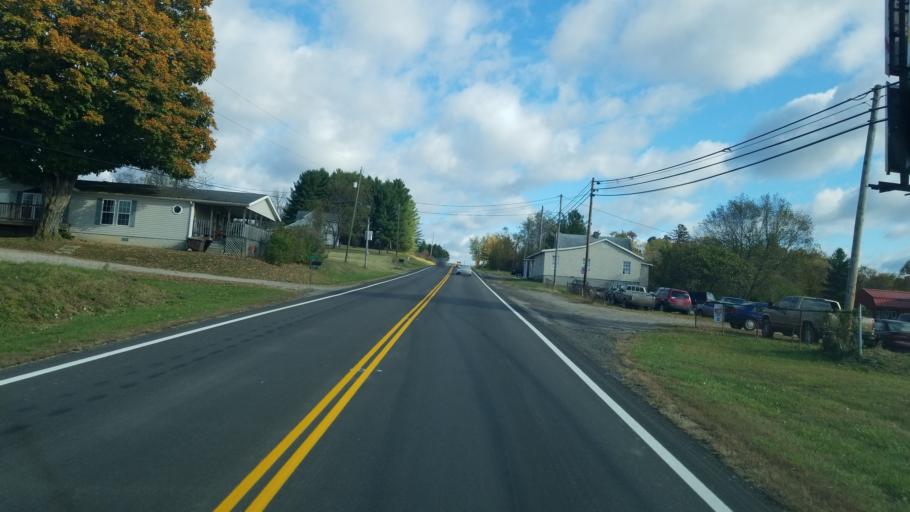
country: US
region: Ohio
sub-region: Jackson County
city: Wellston
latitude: 39.1459
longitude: -82.5311
